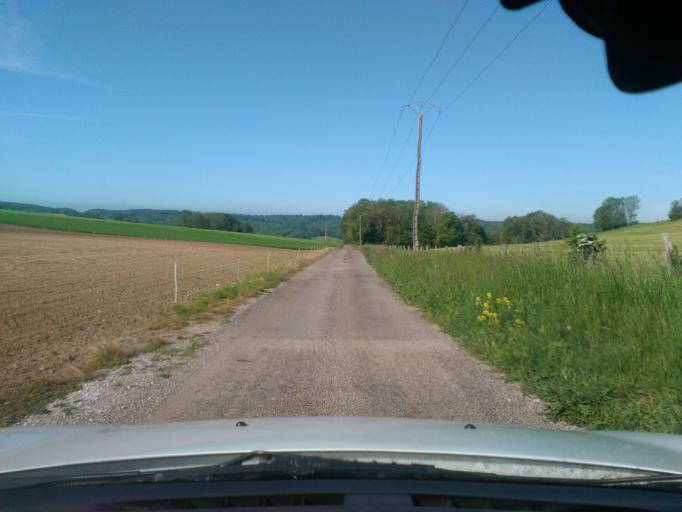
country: FR
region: Lorraine
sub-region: Departement des Vosges
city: Mirecourt
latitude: 48.3266
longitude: 6.2117
